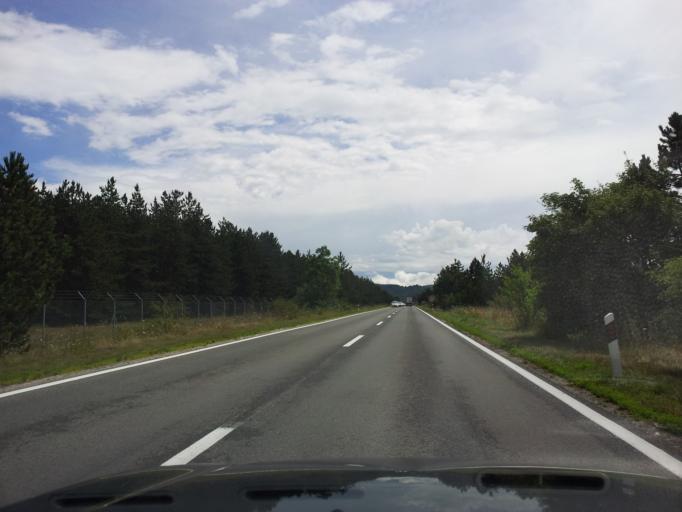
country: HR
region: Zadarska
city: Gracac
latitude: 44.5608
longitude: 15.7578
